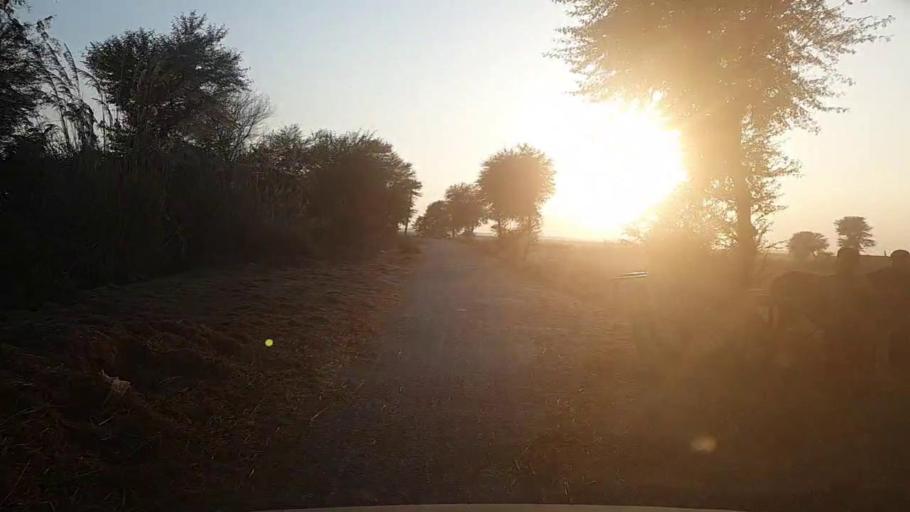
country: PK
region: Sindh
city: Khairpur Nathan Shah
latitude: 27.1812
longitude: 67.7347
